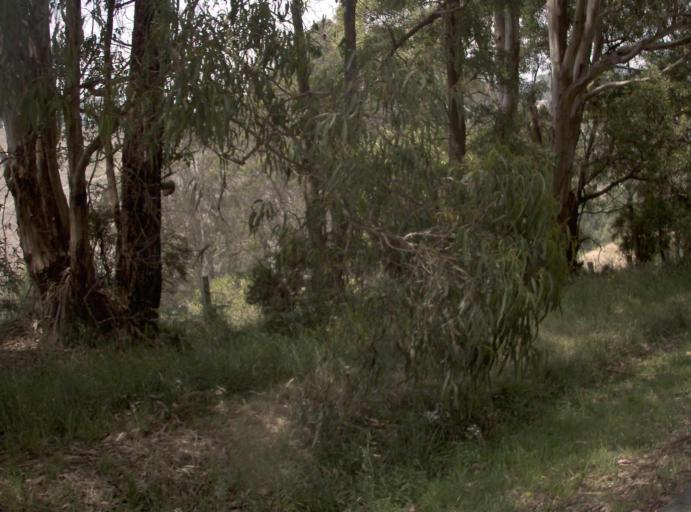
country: AU
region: Victoria
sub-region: Latrobe
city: Traralgon
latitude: -38.3329
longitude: 146.7241
